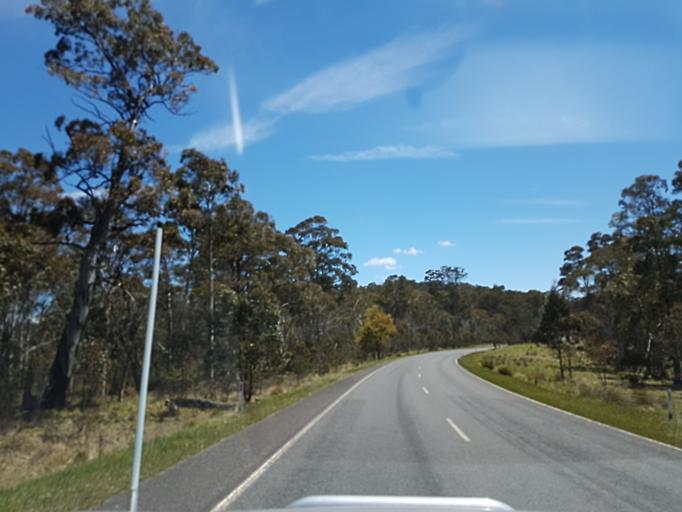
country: AU
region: Victoria
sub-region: Alpine
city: Mount Beauty
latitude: -37.0770
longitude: 147.3523
